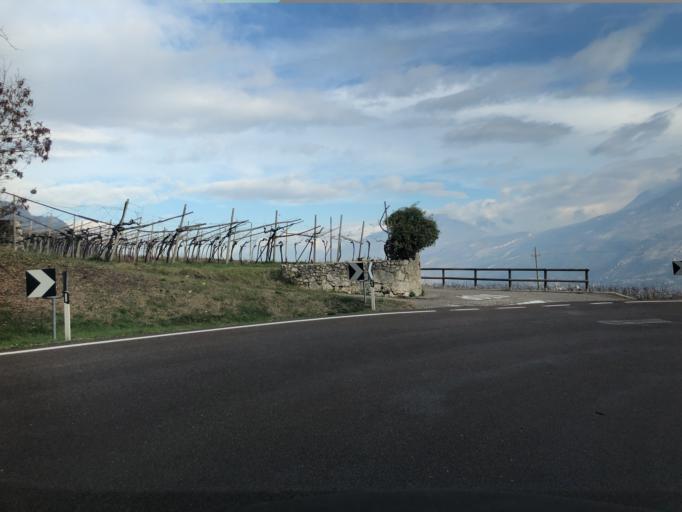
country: IT
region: Trentino-Alto Adige
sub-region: Provincia di Trento
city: Mori
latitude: 45.8404
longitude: 10.9677
